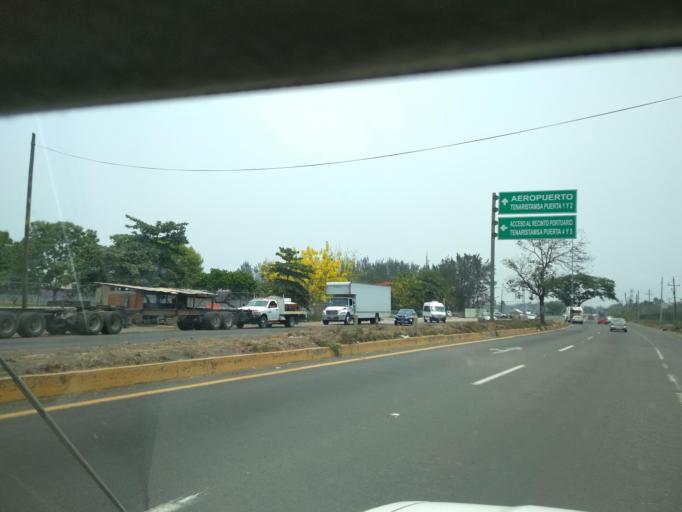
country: MX
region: Veracruz
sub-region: Veracruz
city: Delfino Victoria (Santa Fe)
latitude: 19.1794
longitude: -96.2500
